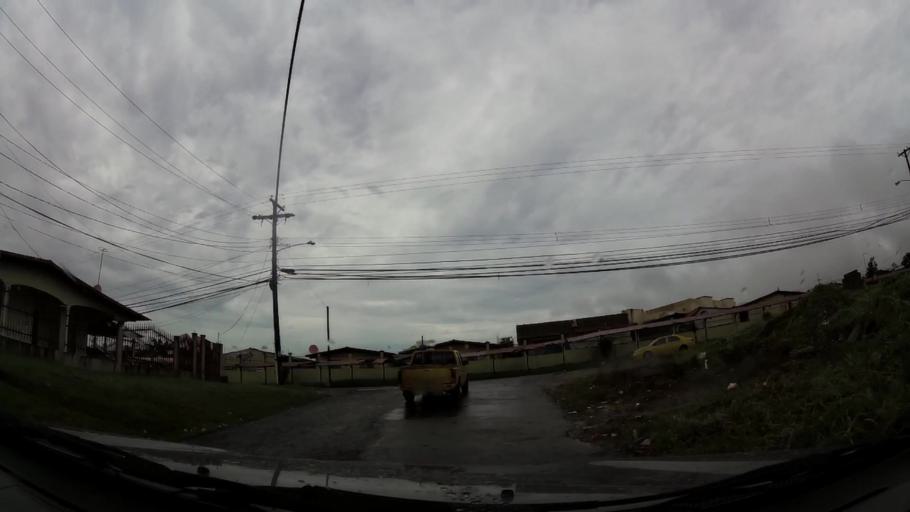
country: PA
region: Colon
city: Arco Iris
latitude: 9.3381
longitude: -79.8718
